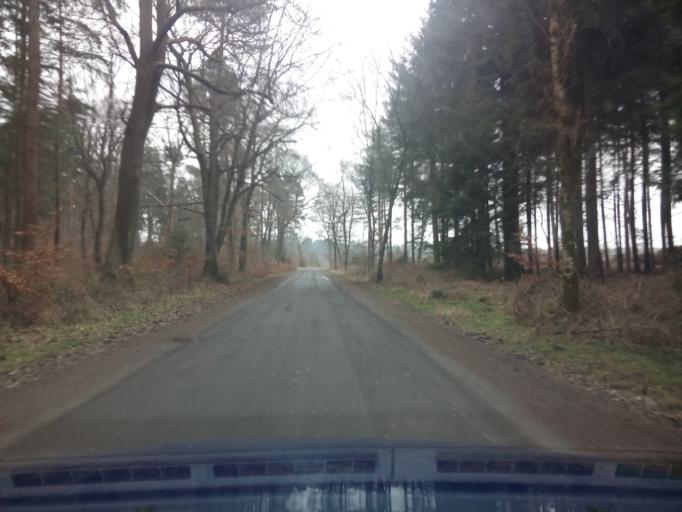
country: DE
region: Lower Saxony
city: Drangstedt
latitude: 53.6142
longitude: 8.7271
